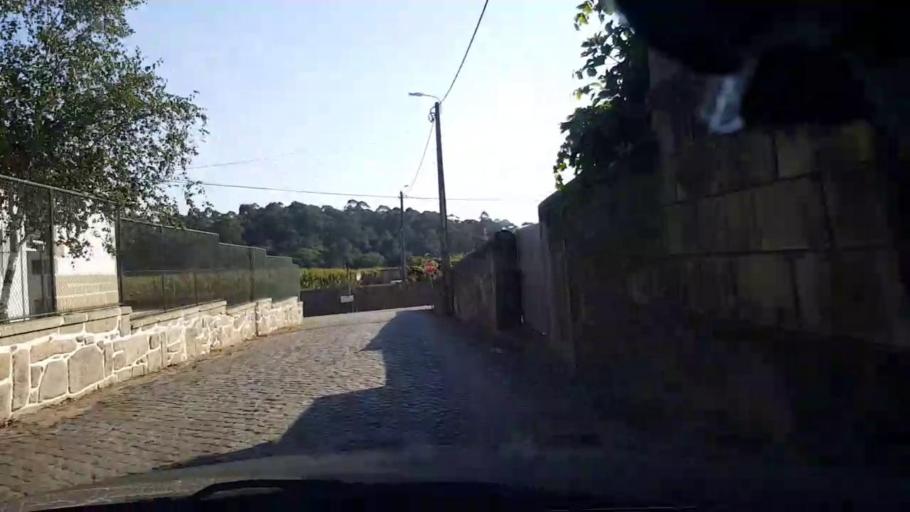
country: PT
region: Porto
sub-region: Vila do Conde
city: Arvore
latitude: 41.3501
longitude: -8.7184
